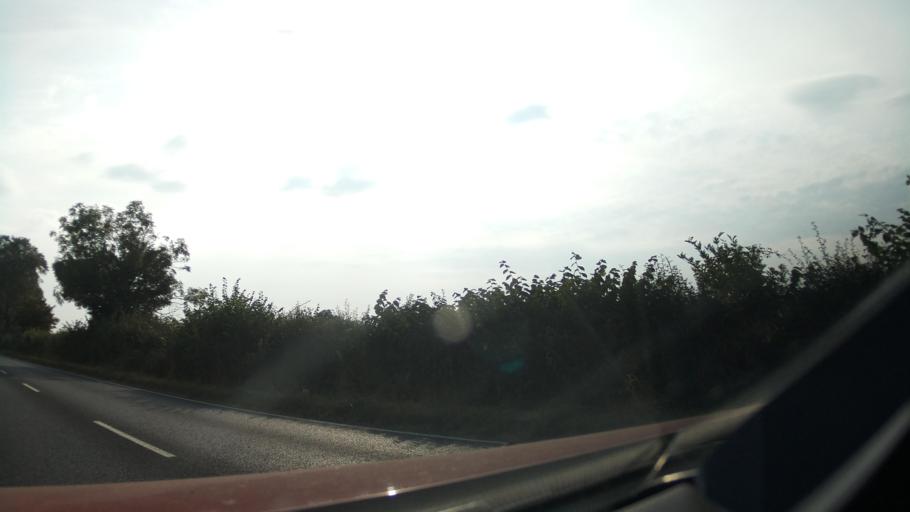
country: GB
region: England
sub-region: Gloucestershire
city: Gotherington
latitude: 51.9926
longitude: -2.0649
